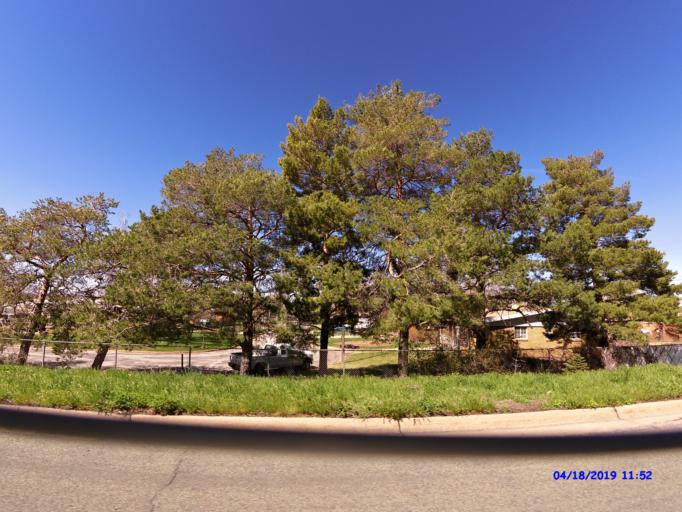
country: US
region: Utah
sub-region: Weber County
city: Ogden
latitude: 41.2478
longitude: -111.9482
